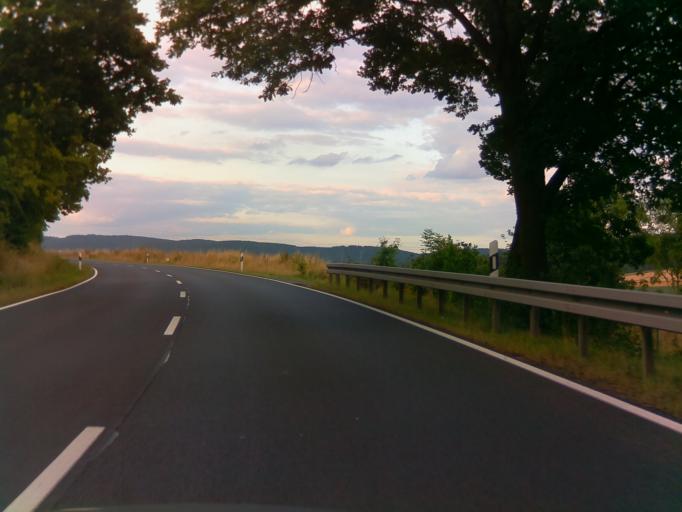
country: DE
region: Hesse
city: Grebenau
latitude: 50.7715
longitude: 9.5300
